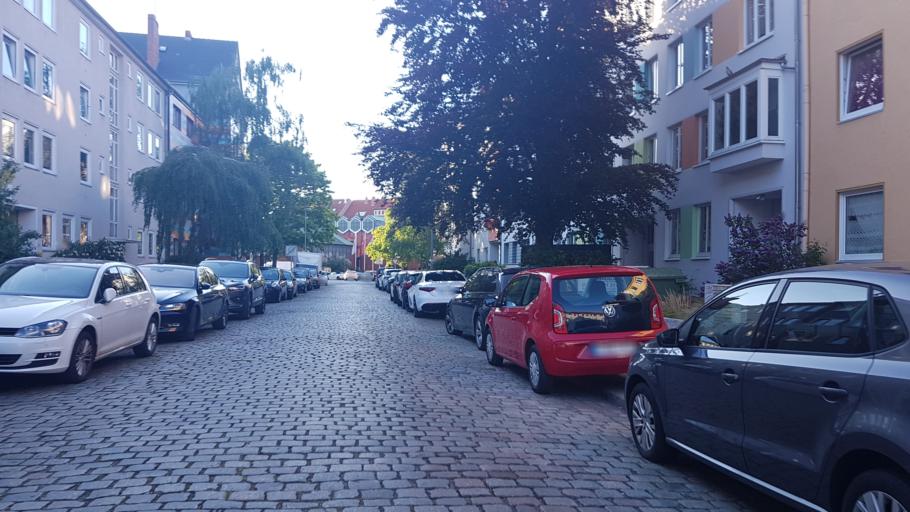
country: DE
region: Lower Saxony
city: Hannover
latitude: 52.3869
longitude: 9.7382
